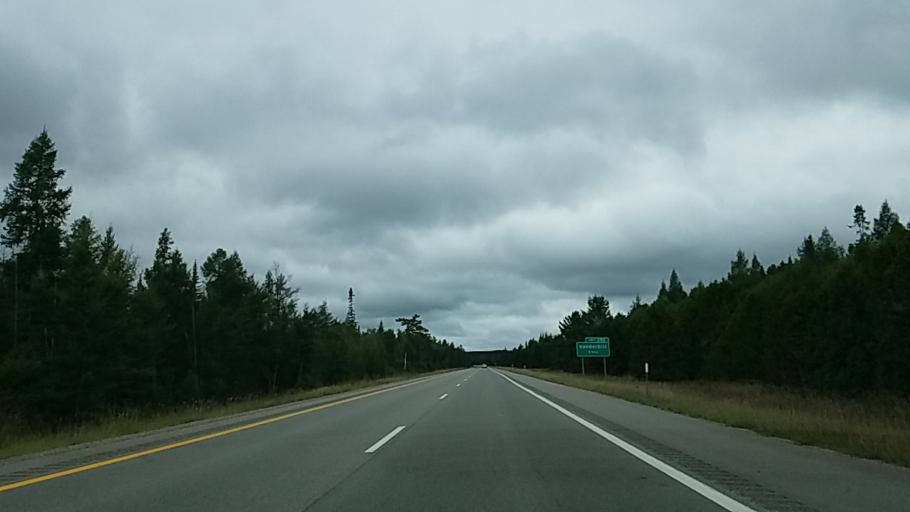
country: US
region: Michigan
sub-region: Otsego County
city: Gaylord
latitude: 45.1669
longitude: -84.6524
